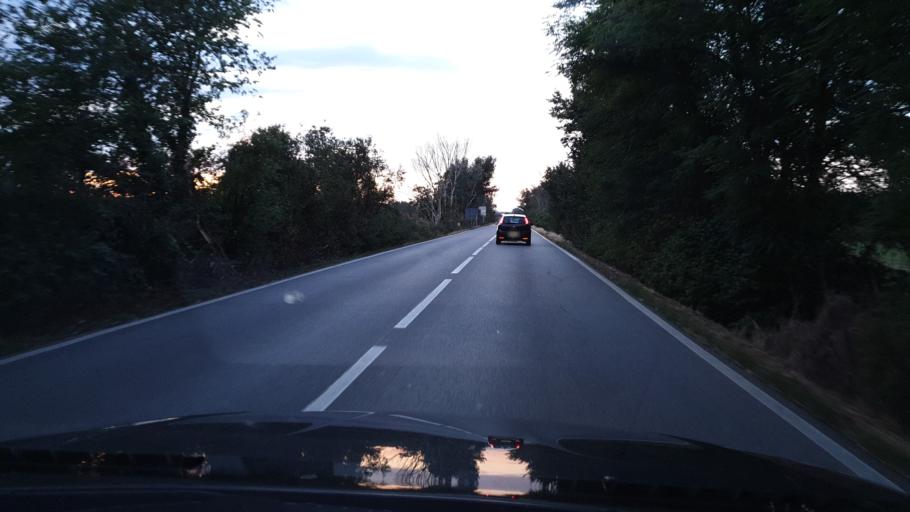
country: IT
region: Emilia-Romagna
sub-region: Provincia di Ravenna
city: Glorie
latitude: 44.4894
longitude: 12.0676
